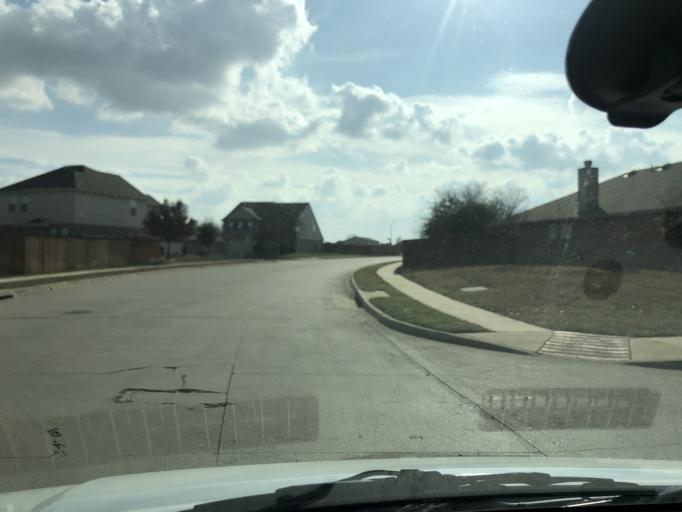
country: US
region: Texas
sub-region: Tarrant County
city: Haslet
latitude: 32.9197
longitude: -97.3660
